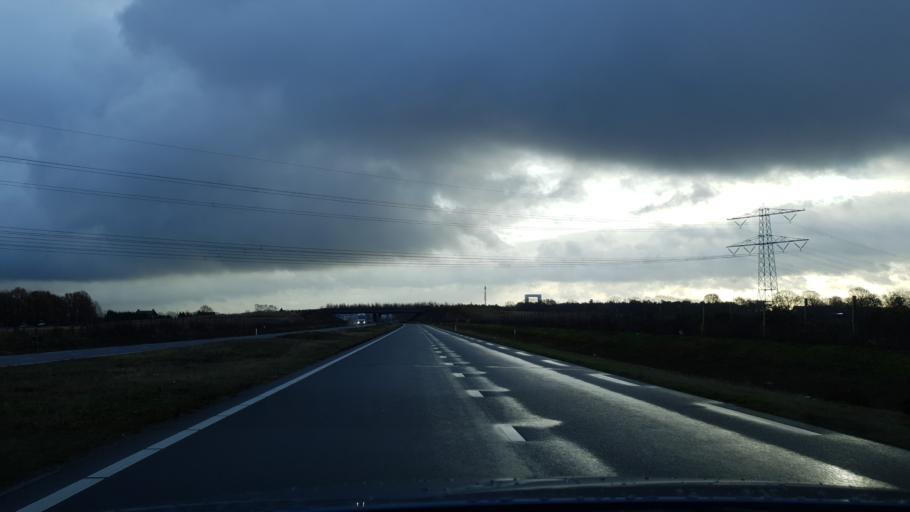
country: NL
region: Limburg
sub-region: Gemeente Venlo
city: Tegelen
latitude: 51.4121
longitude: 6.1036
